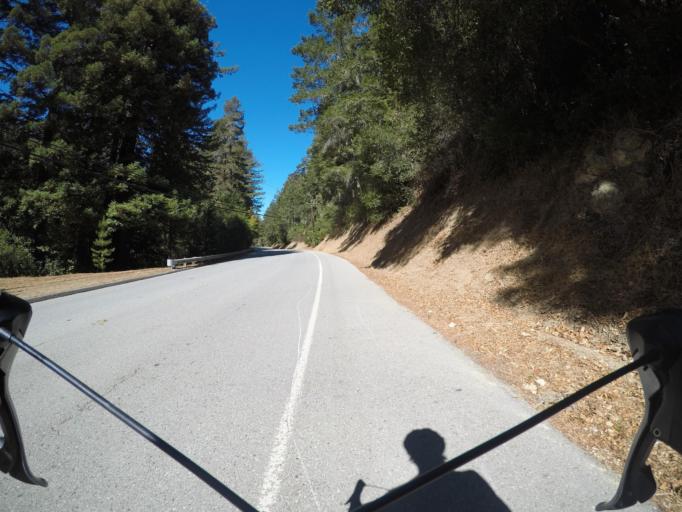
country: US
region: California
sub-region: San Mateo County
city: Portola Valley
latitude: 37.3071
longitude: -122.2700
